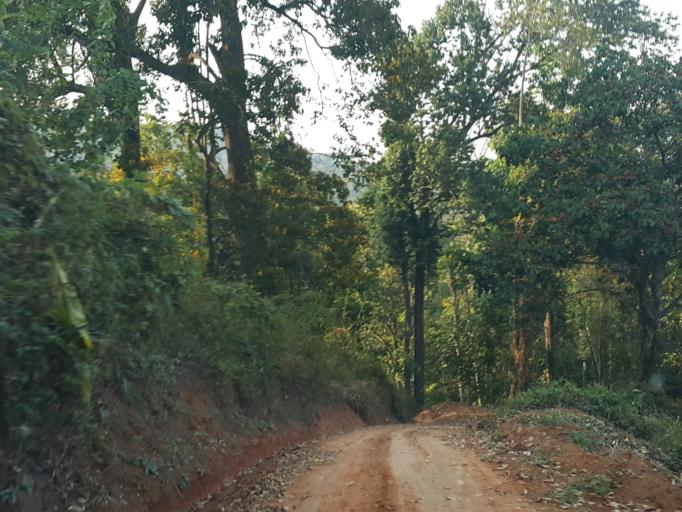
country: TH
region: Chiang Mai
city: Mae Taeng
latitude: 19.0445
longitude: 98.7678
